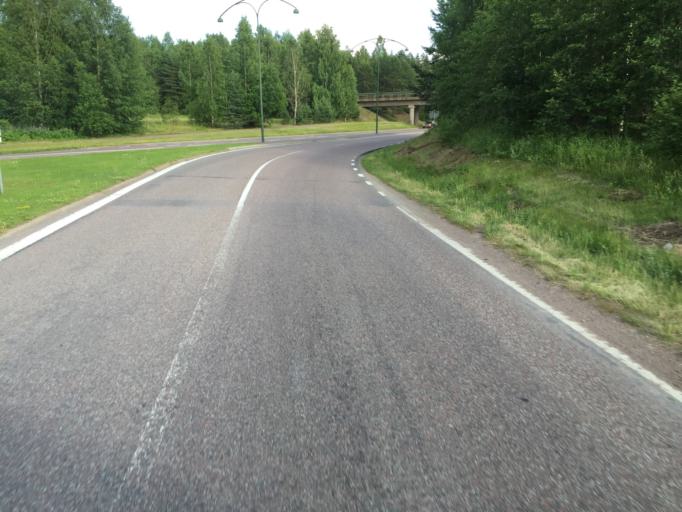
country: SE
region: Dalarna
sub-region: Borlange Kommun
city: Borlaenge
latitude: 60.5057
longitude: 15.3870
